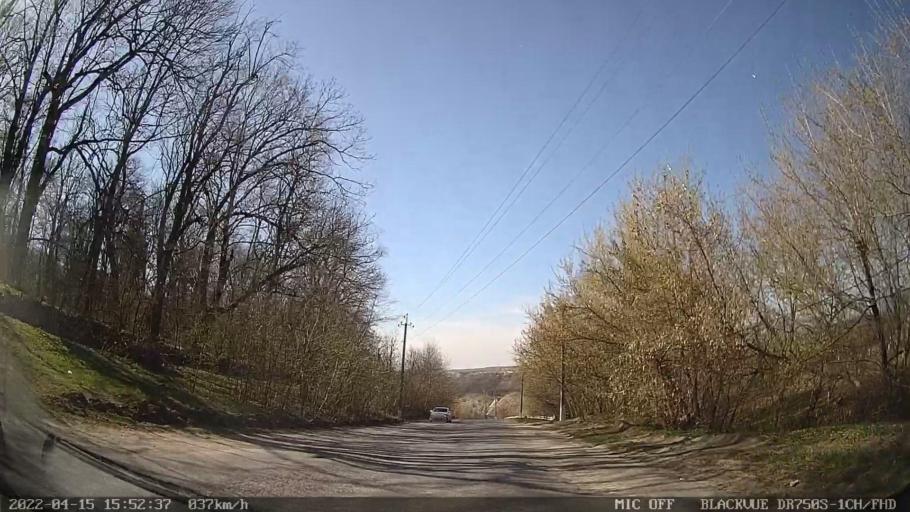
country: MD
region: Raionul Ocnita
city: Otaci
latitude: 48.3954
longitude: 27.8915
